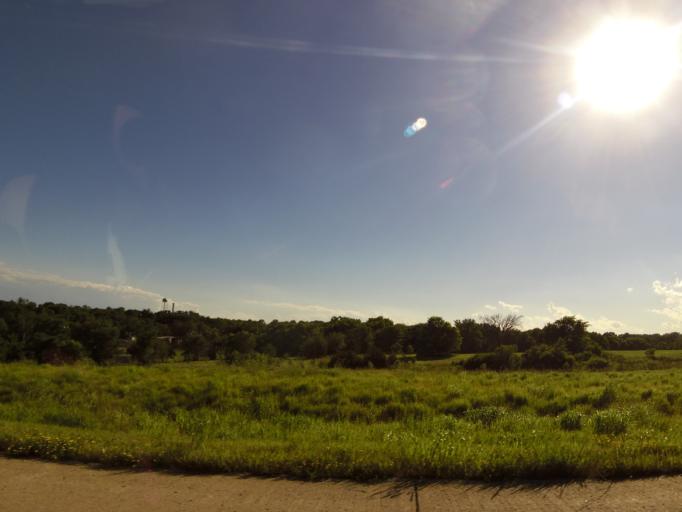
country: US
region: Missouri
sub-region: Ralls County
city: New London
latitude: 39.4998
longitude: -91.3182
